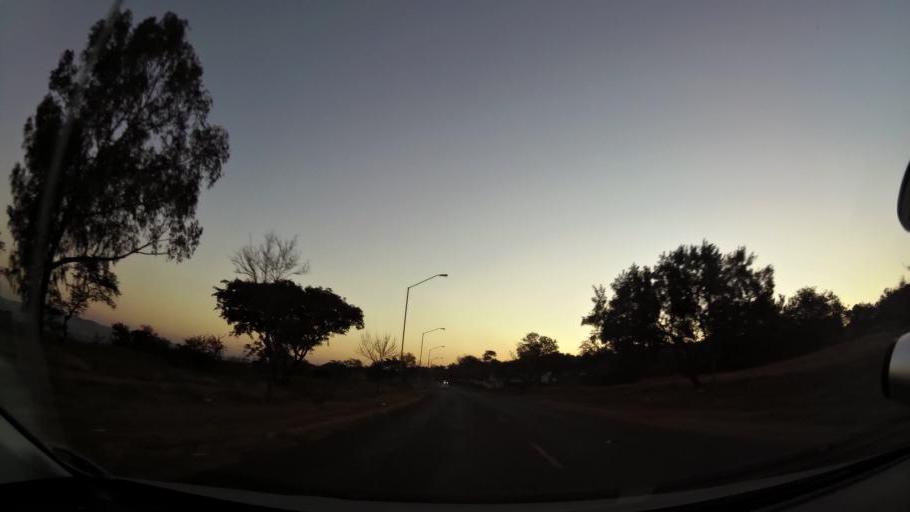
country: ZA
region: Gauteng
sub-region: City of Tshwane Metropolitan Municipality
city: Pretoria
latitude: -25.7311
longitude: 28.1357
